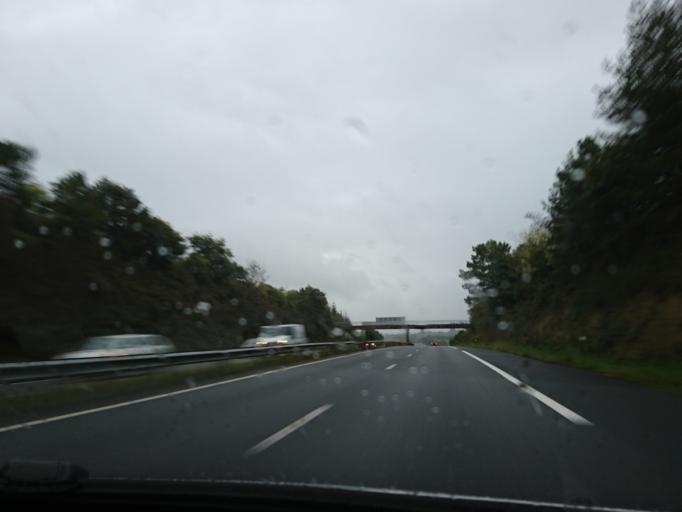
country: FR
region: Brittany
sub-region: Departement du Finistere
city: Hopital-Camfrout
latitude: 48.3294
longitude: -4.2276
